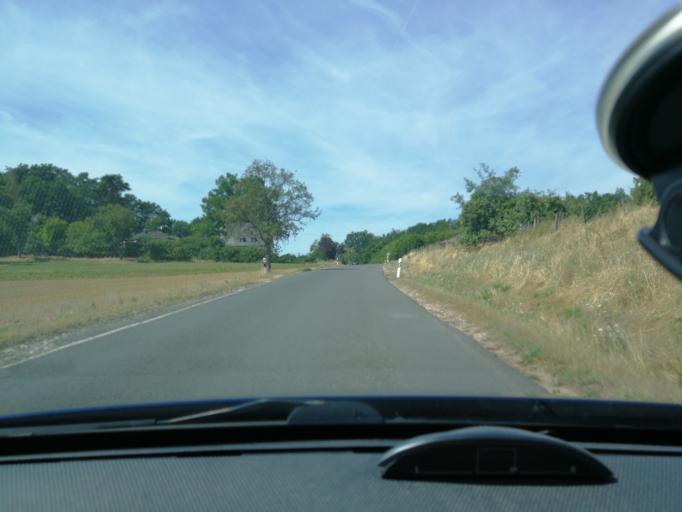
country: DE
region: Rheinland-Pfalz
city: Niersbach
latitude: 49.9370
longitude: 6.7483
